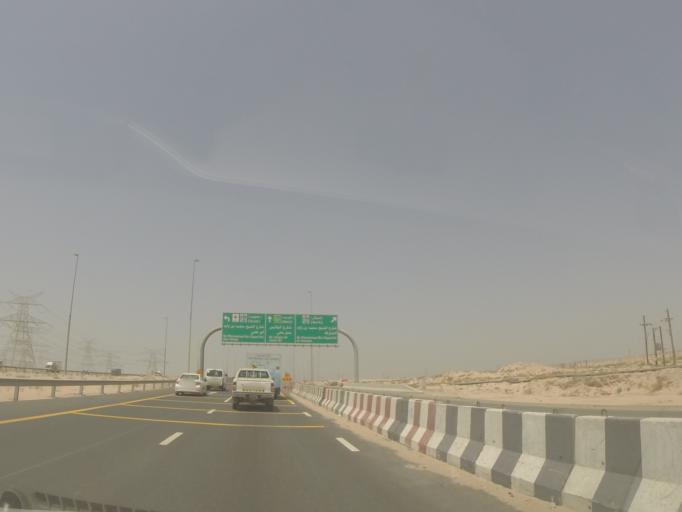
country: AE
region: Dubai
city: Dubai
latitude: 25.0112
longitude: 55.1668
